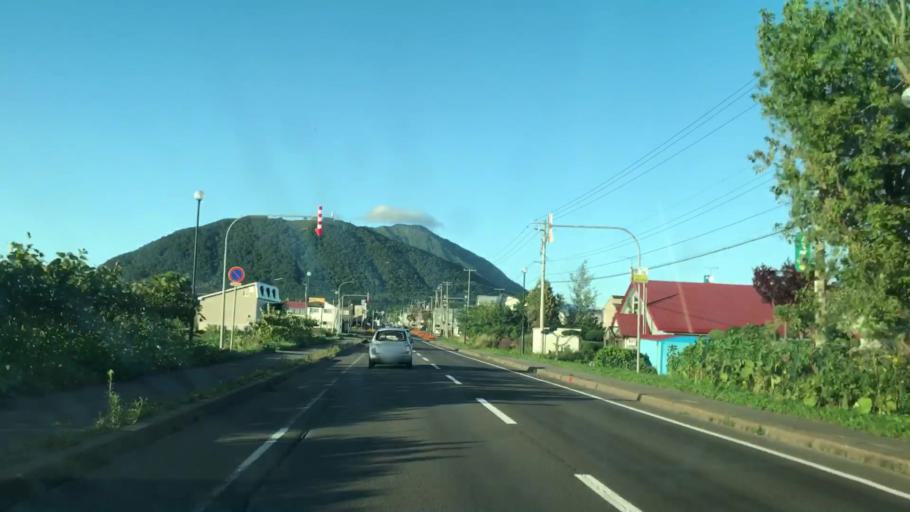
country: JP
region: Hokkaido
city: Niseko Town
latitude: 42.7312
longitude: 140.8712
